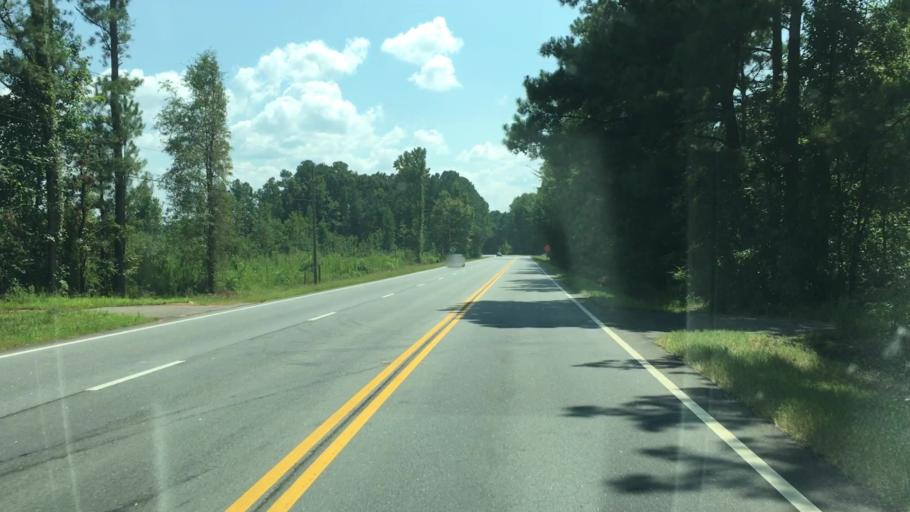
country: US
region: Georgia
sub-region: Oconee County
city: Watkinsville
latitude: 33.7347
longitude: -83.4297
